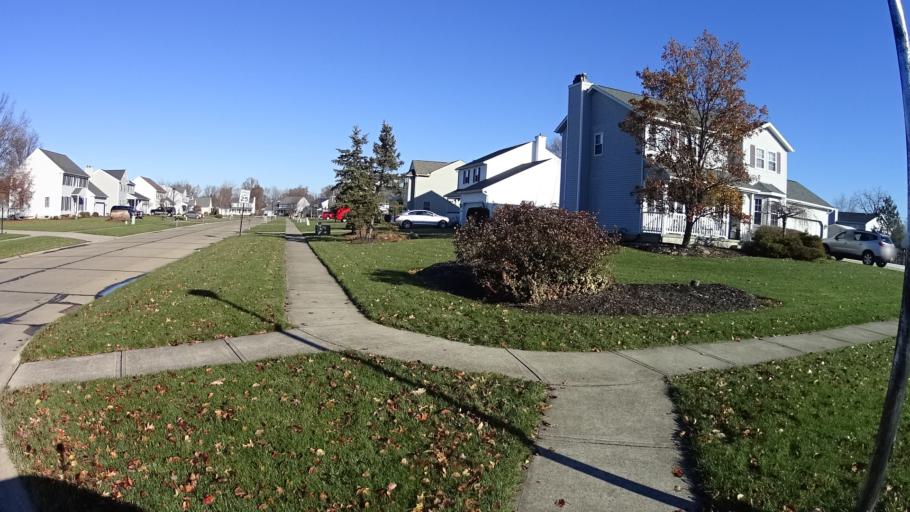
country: US
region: Ohio
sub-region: Lorain County
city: North Ridgeville
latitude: 41.4124
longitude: -82.0080
